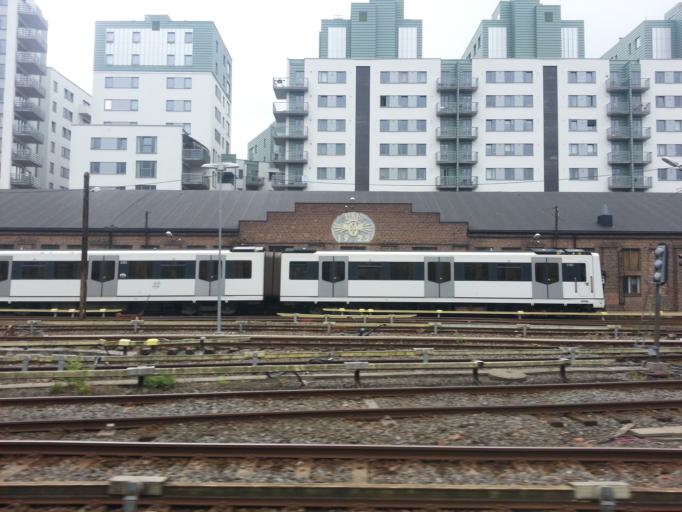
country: NO
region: Oslo
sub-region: Oslo
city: Sjolyststranda
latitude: 59.9318
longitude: 10.7123
